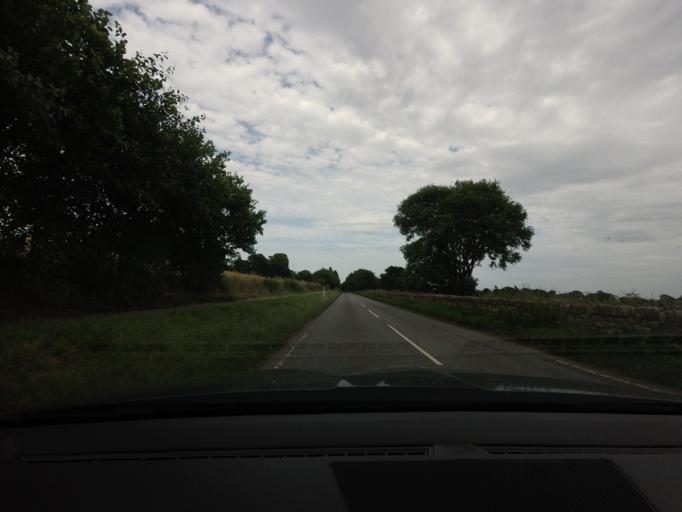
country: GB
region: Scotland
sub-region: Highland
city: Alness
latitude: 57.6892
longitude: -4.2780
